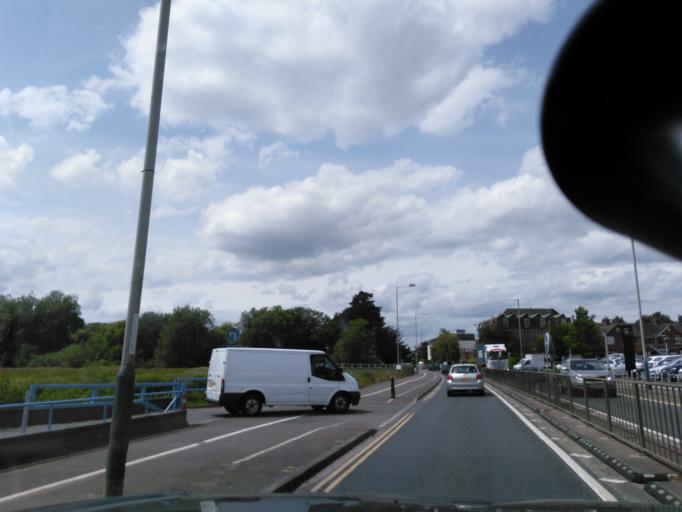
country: GB
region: England
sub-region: Wiltshire
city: Salisbury
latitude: 51.0636
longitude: -1.7835
